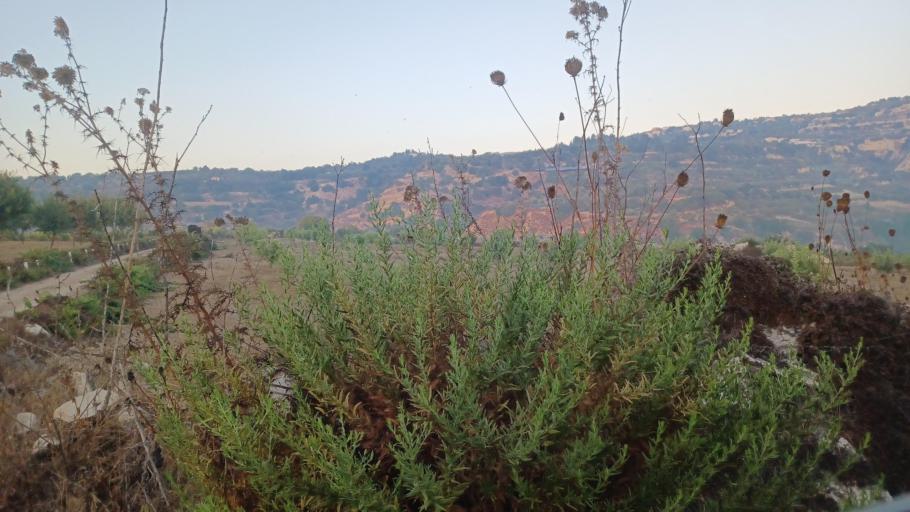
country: CY
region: Pafos
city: Mesogi
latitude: 34.8476
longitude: 32.5145
